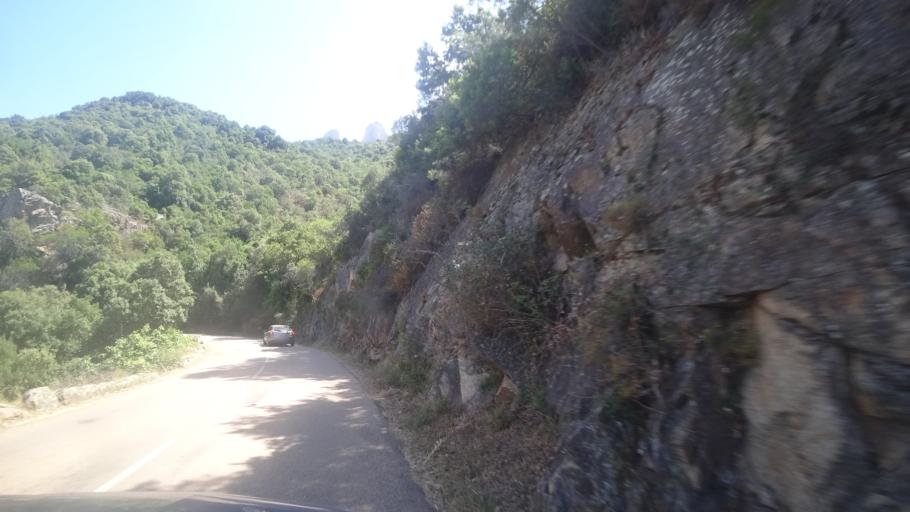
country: FR
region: Corsica
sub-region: Departement de la Corse-du-Sud
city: Cargese
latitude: 42.2624
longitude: 8.6945
